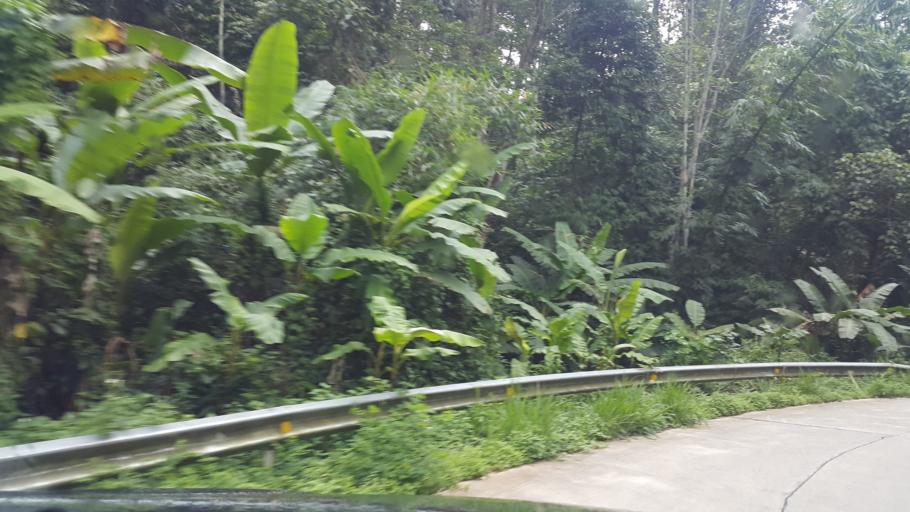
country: TH
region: Lampang
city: Wang Nuea
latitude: 19.0767
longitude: 99.3868
